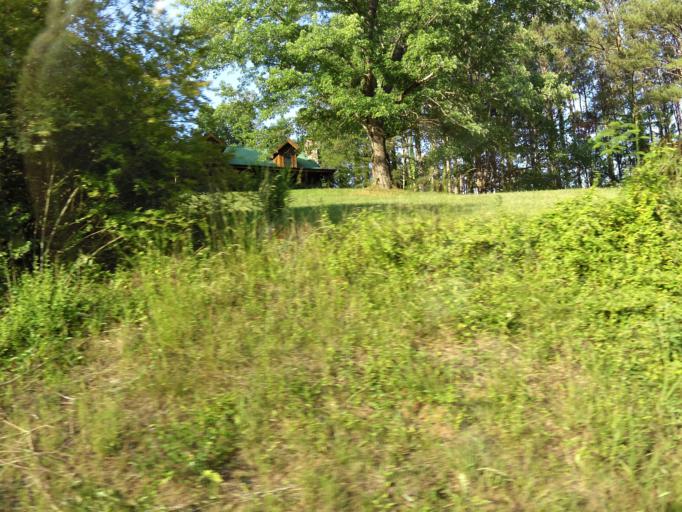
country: US
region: Tennessee
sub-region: Sevier County
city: Sevierville
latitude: 35.8290
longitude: -83.6113
